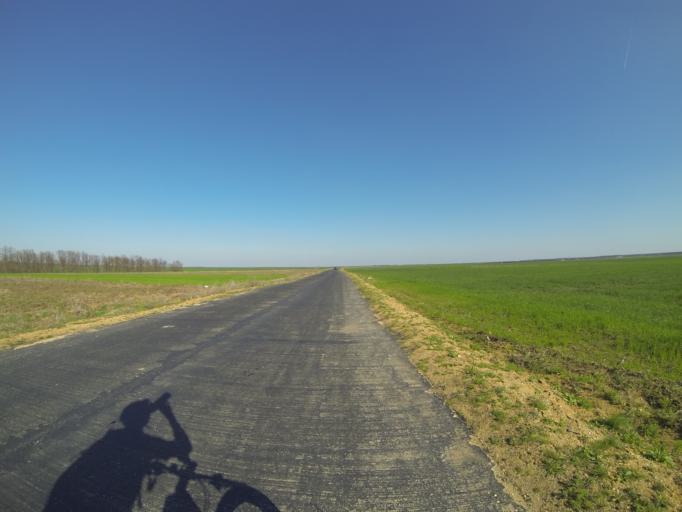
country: RO
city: Varvoru
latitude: 44.2269
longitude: 23.6702
